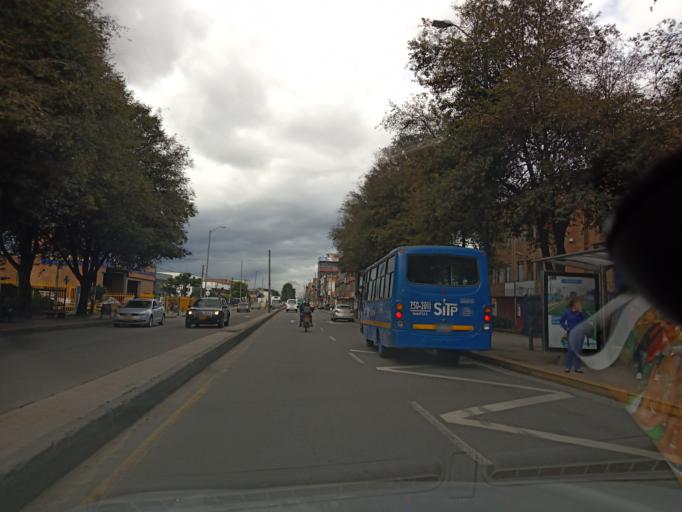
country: CO
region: Cundinamarca
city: Funza
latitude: 4.6843
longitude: -74.1317
